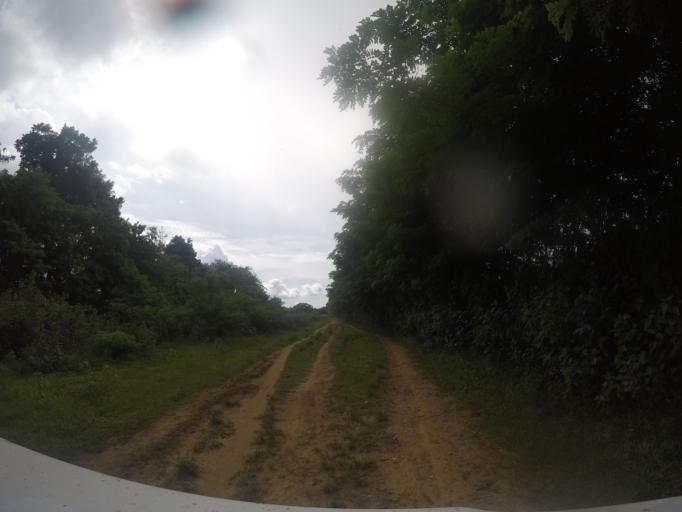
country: TL
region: Lautem
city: Lospalos
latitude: -8.5069
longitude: 127.0123
